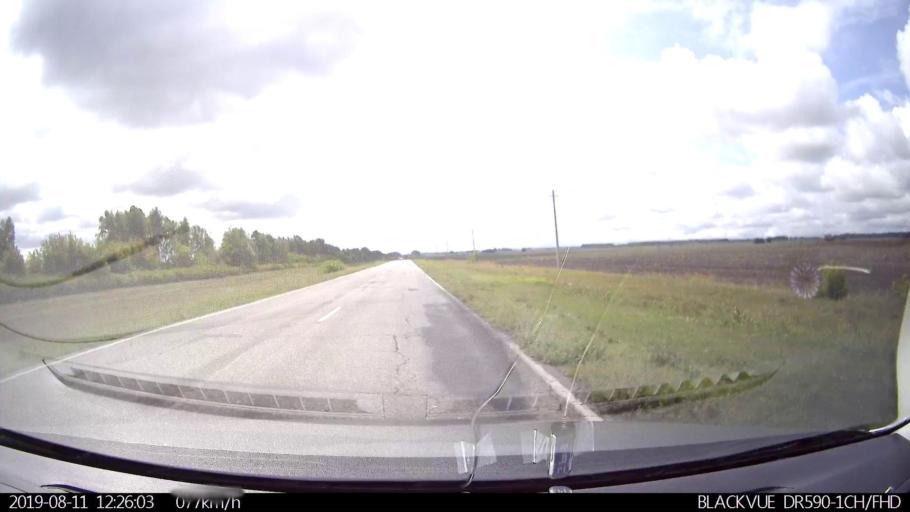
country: RU
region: Ulyanovsk
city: Ignatovka
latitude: 53.8677
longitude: 47.9344
